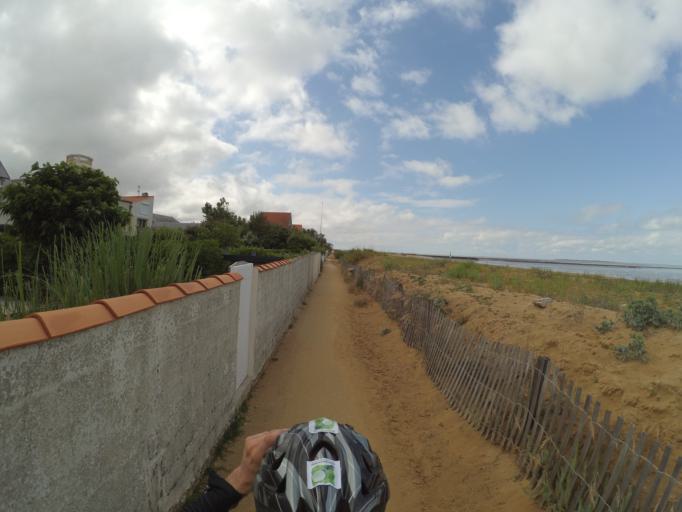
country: FR
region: Poitou-Charentes
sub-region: Departement de la Charente-Maritime
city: Chatelaillon-Plage
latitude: 46.0676
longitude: -1.0929
